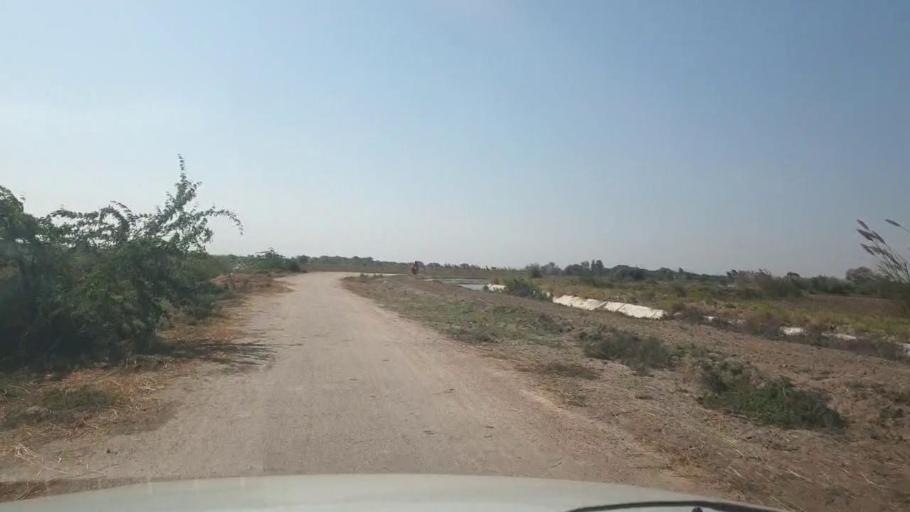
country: PK
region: Sindh
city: Mirpur Sakro
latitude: 24.4217
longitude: 67.7896
